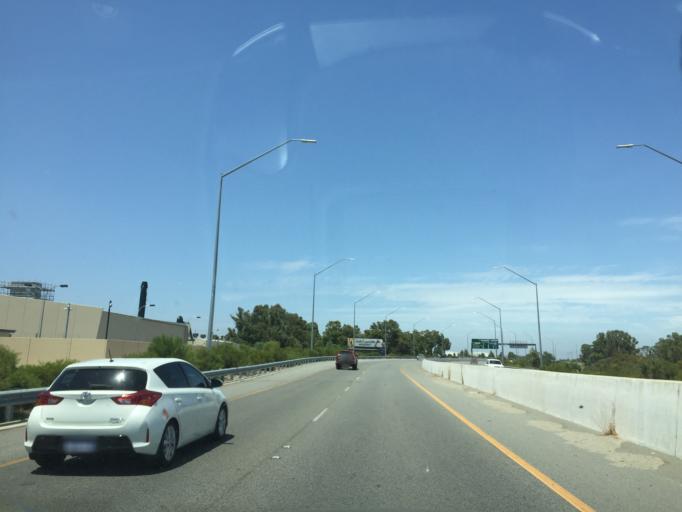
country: AU
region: Western Australia
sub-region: Belmont
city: Kewdale
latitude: -31.9594
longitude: 115.9679
